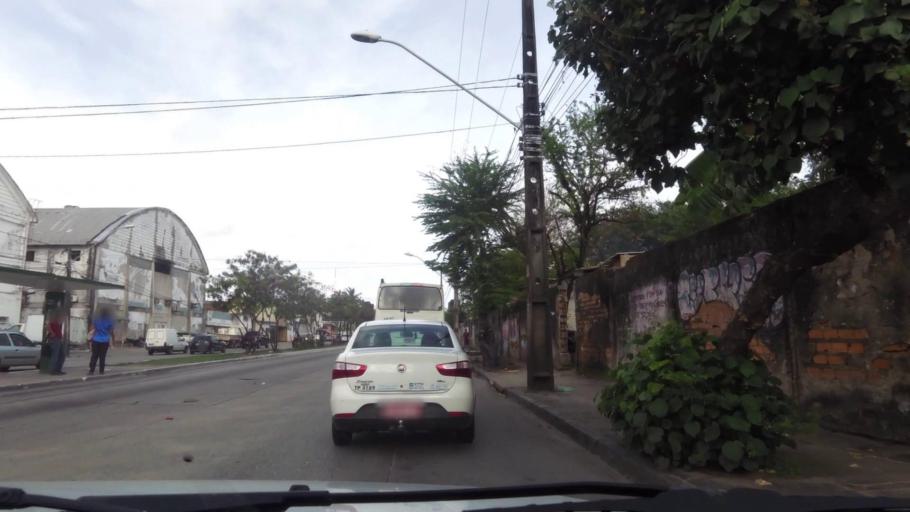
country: BR
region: Pernambuco
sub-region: Recife
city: Recife
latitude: -8.0777
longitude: -34.8971
